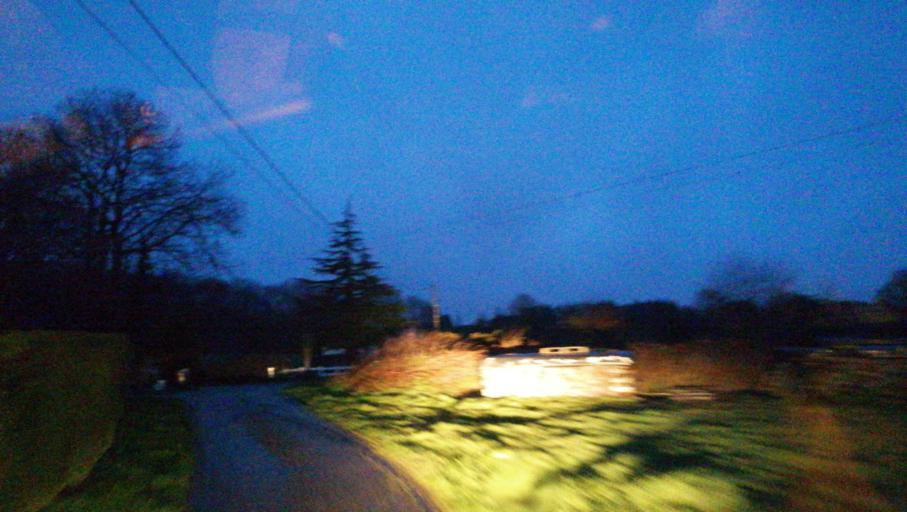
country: FR
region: Brittany
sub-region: Departement des Cotes-d'Armor
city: Plouagat
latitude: 48.4811
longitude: -2.9685
